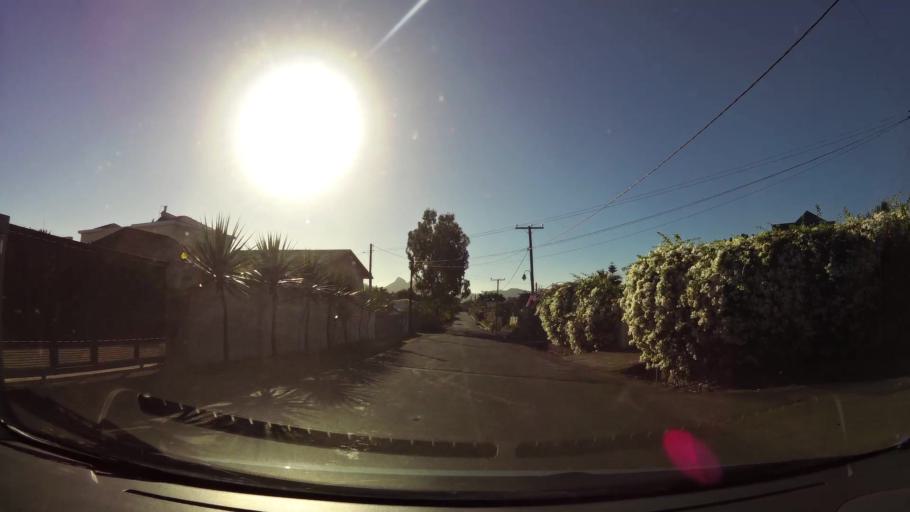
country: MU
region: Black River
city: Tamarin
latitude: -20.3358
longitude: 57.3764
